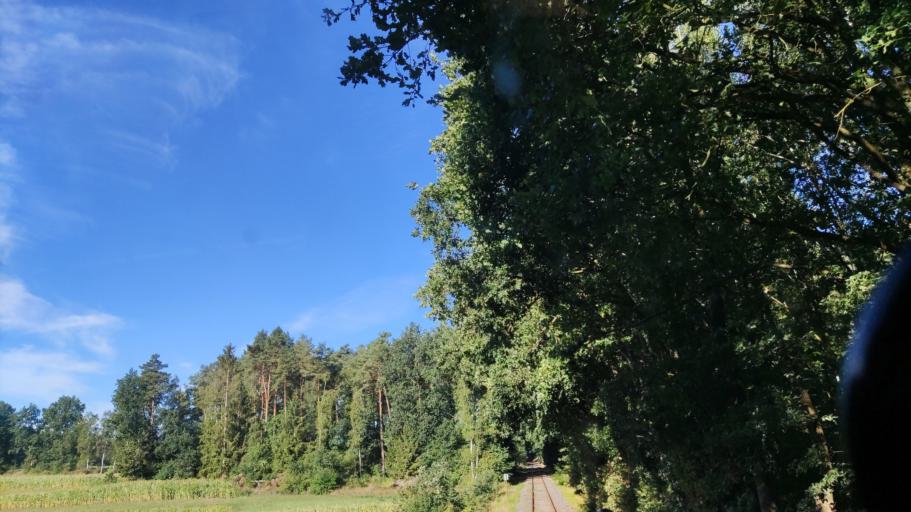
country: DE
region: Lower Saxony
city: Soderstorf
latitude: 53.1399
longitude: 10.1639
